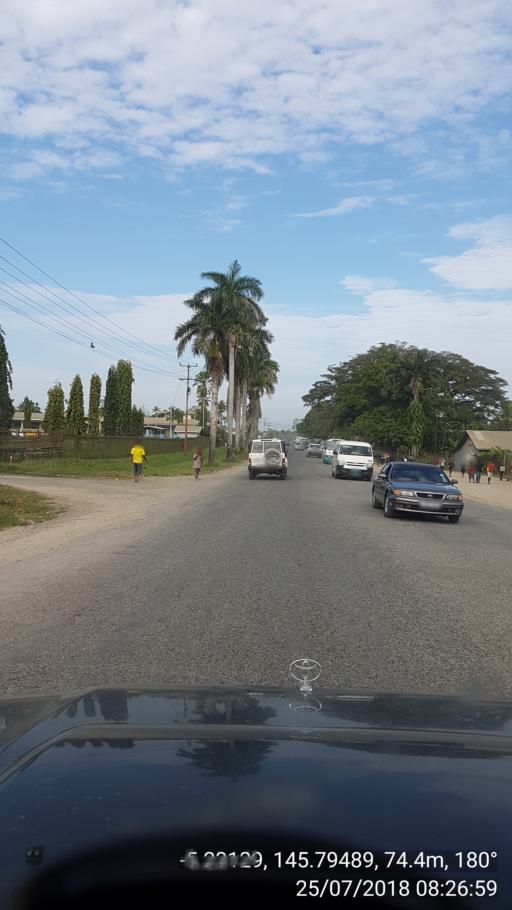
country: PG
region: Madang
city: Madang
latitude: -5.2311
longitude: 145.7950
